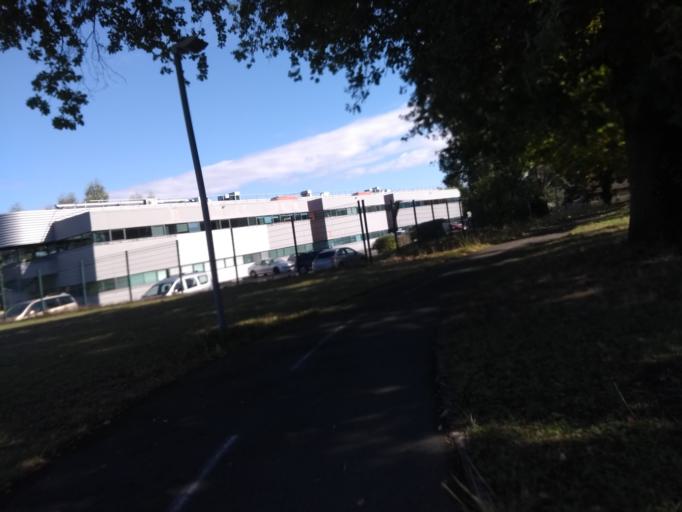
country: FR
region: Aquitaine
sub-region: Departement de la Gironde
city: Pessac
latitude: 44.7939
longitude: -0.6257
